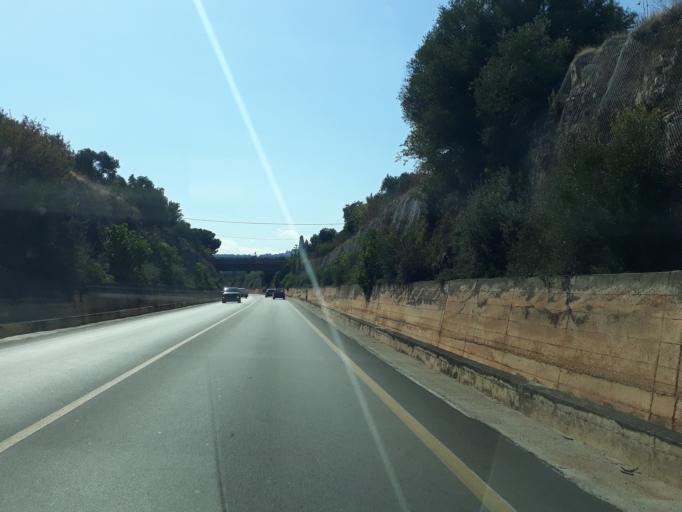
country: IT
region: Apulia
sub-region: Provincia di Brindisi
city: Fasano
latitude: 40.8387
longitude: 17.3514
